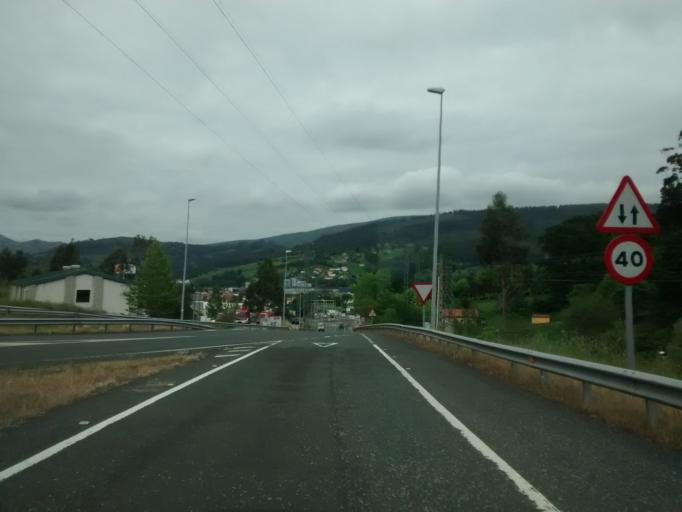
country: ES
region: Cantabria
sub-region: Provincia de Cantabria
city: Los Corrales de Buelna
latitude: 43.2513
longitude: -4.0743
